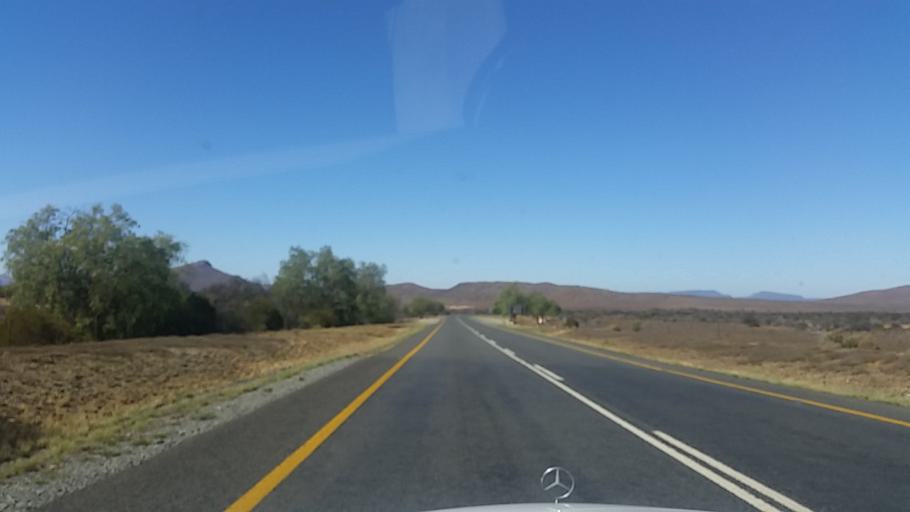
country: ZA
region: Eastern Cape
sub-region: Cacadu District Municipality
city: Graaff-Reinet
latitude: -32.0676
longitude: 24.6059
